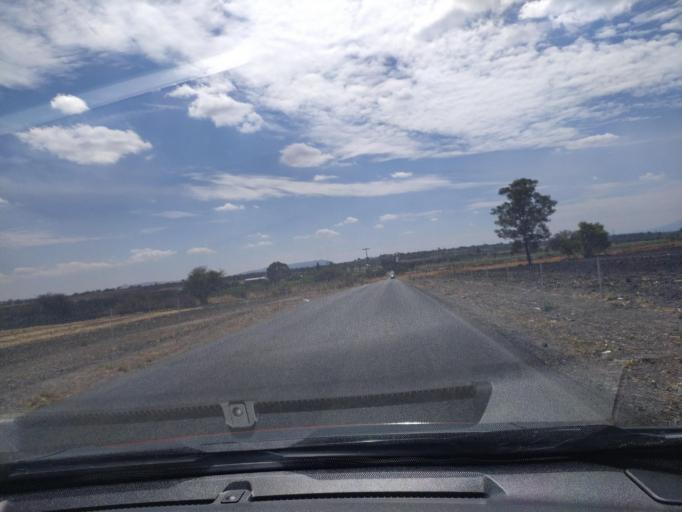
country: MX
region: Guanajuato
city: San Roque
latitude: 20.9606
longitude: -101.8301
